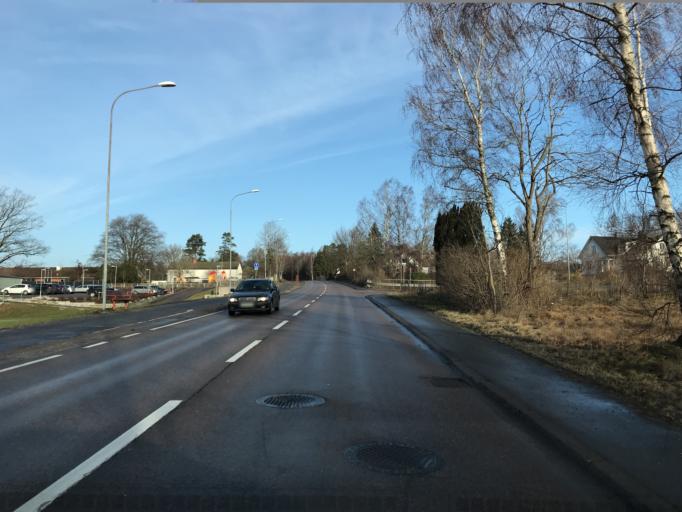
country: SE
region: Skane
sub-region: Hassleholms Kommun
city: Bjarnum
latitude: 56.2949
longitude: 13.7080
